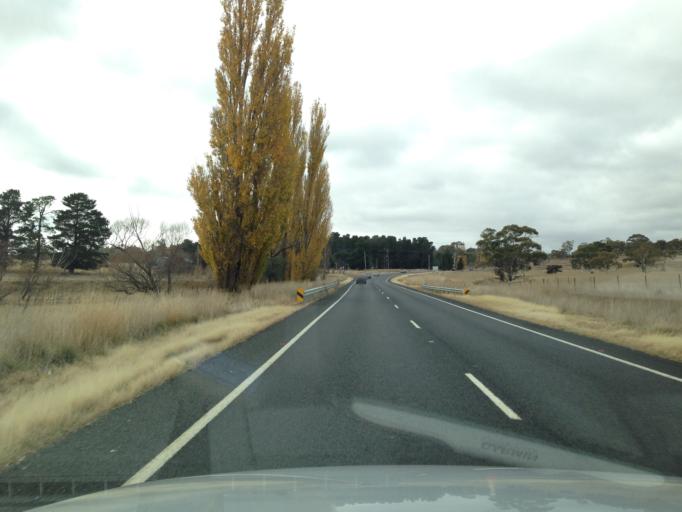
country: AU
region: New South Wales
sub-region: Cooma-Monaro
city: Cooma
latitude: -36.2422
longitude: 149.0640
